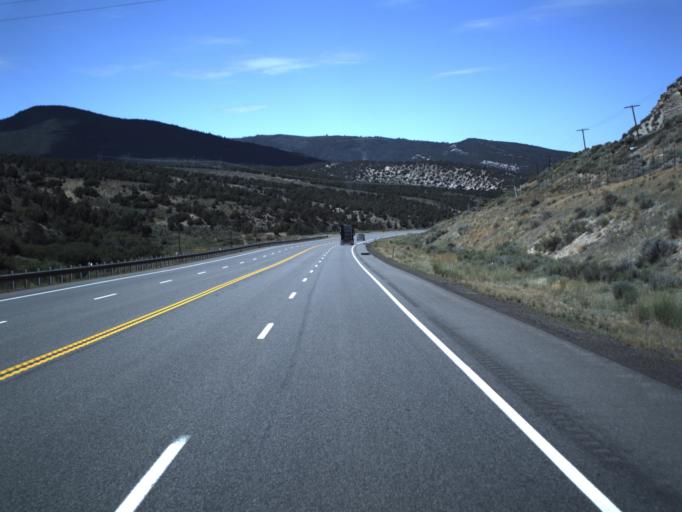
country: US
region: Utah
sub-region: Sanpete County
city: Fairview
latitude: 39.9294
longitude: -111.1796
